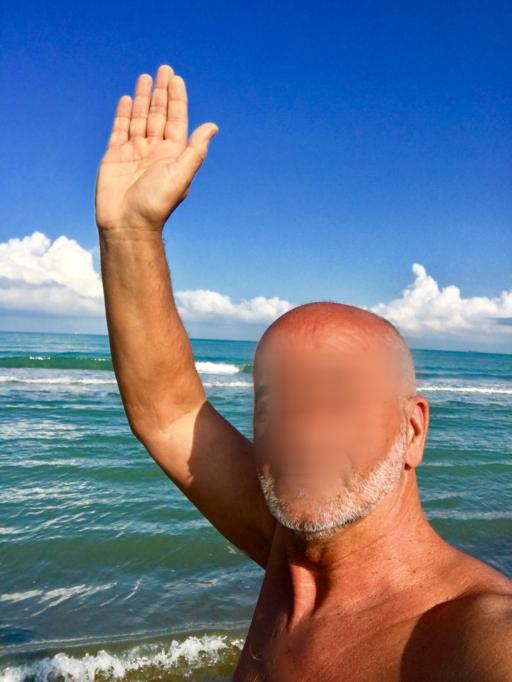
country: AL
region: Tirane
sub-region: Rrethi i Kavajes
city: Golem
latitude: 41.2573
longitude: 19.5192
